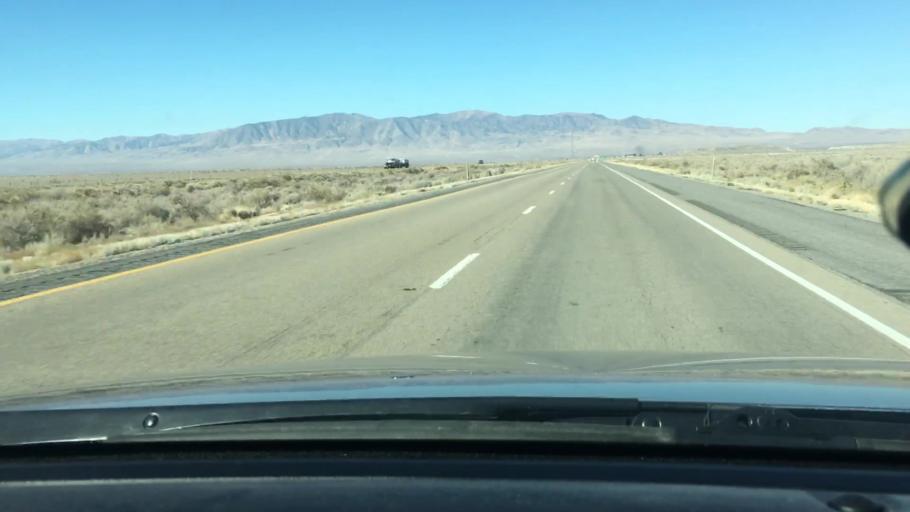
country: US
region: Utah
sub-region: Tooele County
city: Grantsville
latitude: 40.7548
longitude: -112.7403
